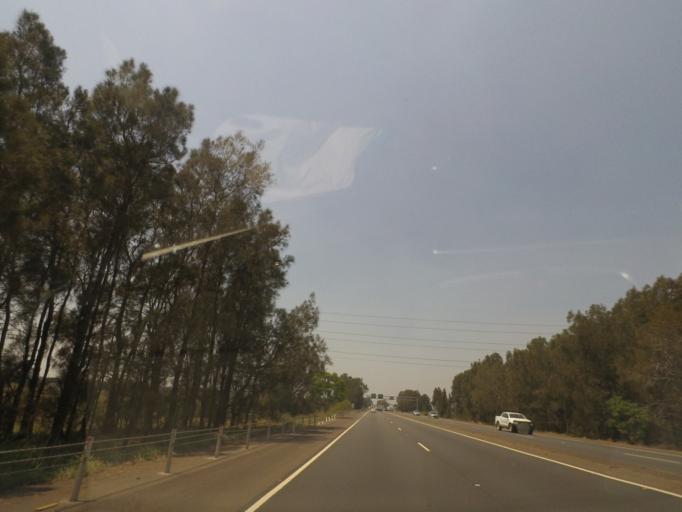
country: AU
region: New South Wales
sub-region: Newcastle
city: Beresfield
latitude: -32.8125
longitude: 151.6759
